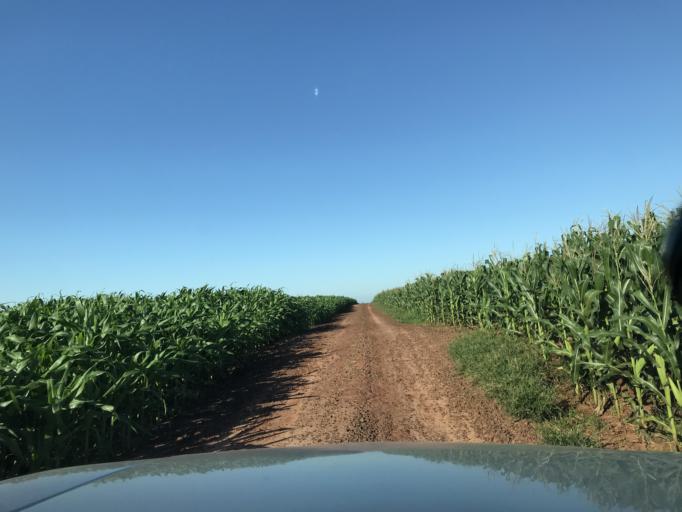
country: BR
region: Parana
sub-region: Palotina
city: Palotina
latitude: -24.2308
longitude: -53.7627
